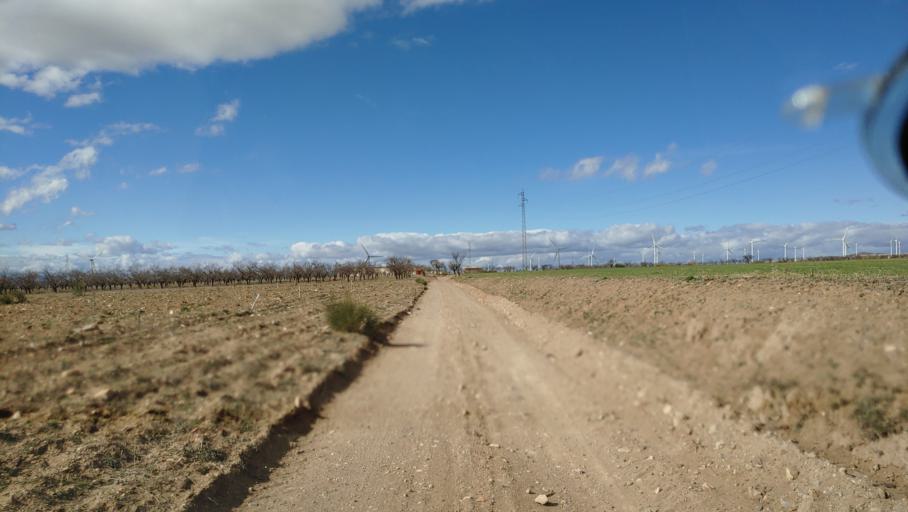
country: ES
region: Andalusia
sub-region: Provincia de Granada
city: Hueneja
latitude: 37.2264
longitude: -2.9583
